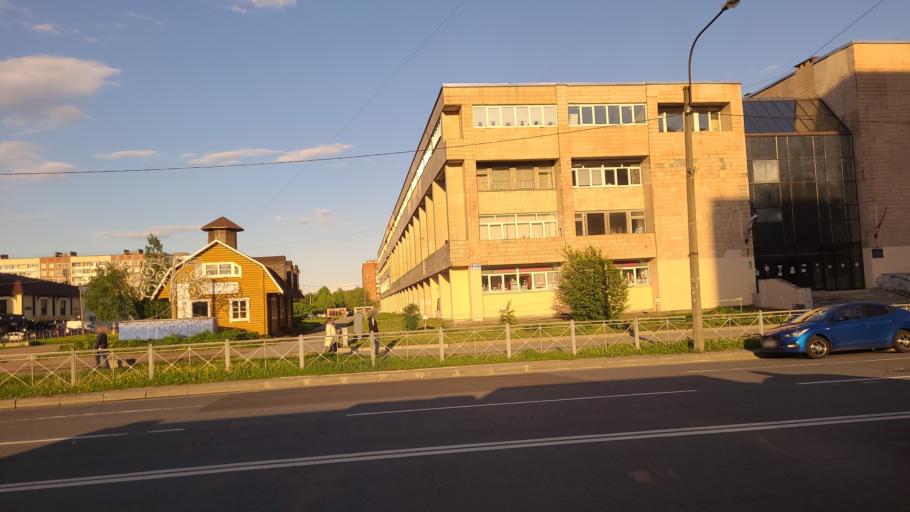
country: RU
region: St.-Petersburg
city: Kolpino
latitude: 59.7351
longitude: 30.5790
